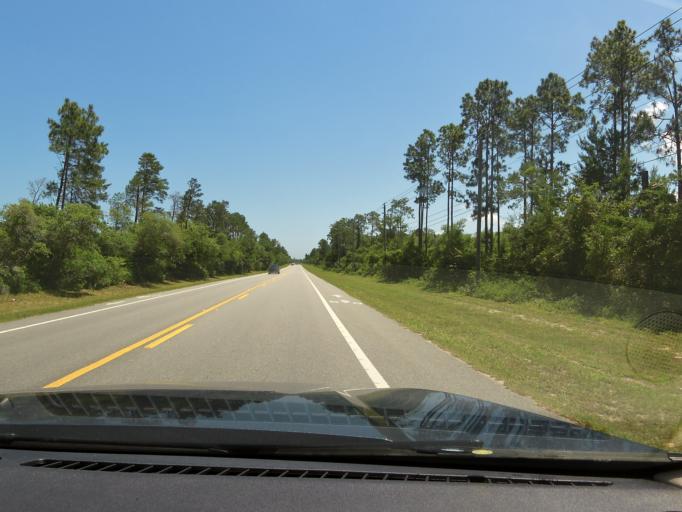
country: US
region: Florida
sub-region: Flagler County
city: Flagler Beach
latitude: 29.4475
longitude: -81.1636
